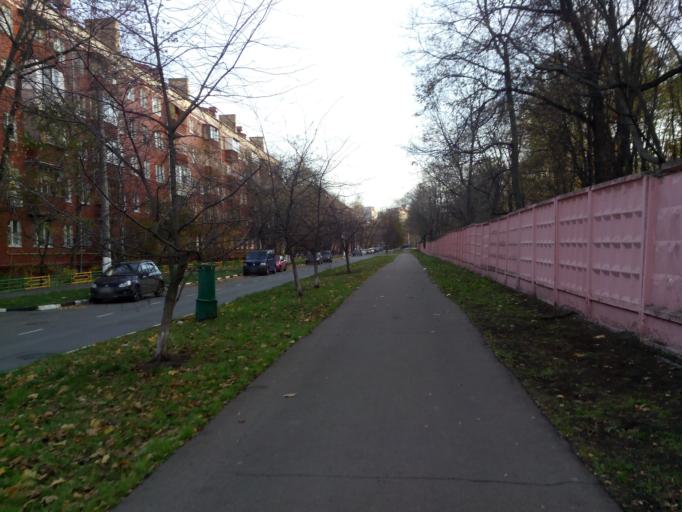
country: RU
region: Moscow
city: Lefortovo
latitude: 55.7710
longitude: 37.7087
